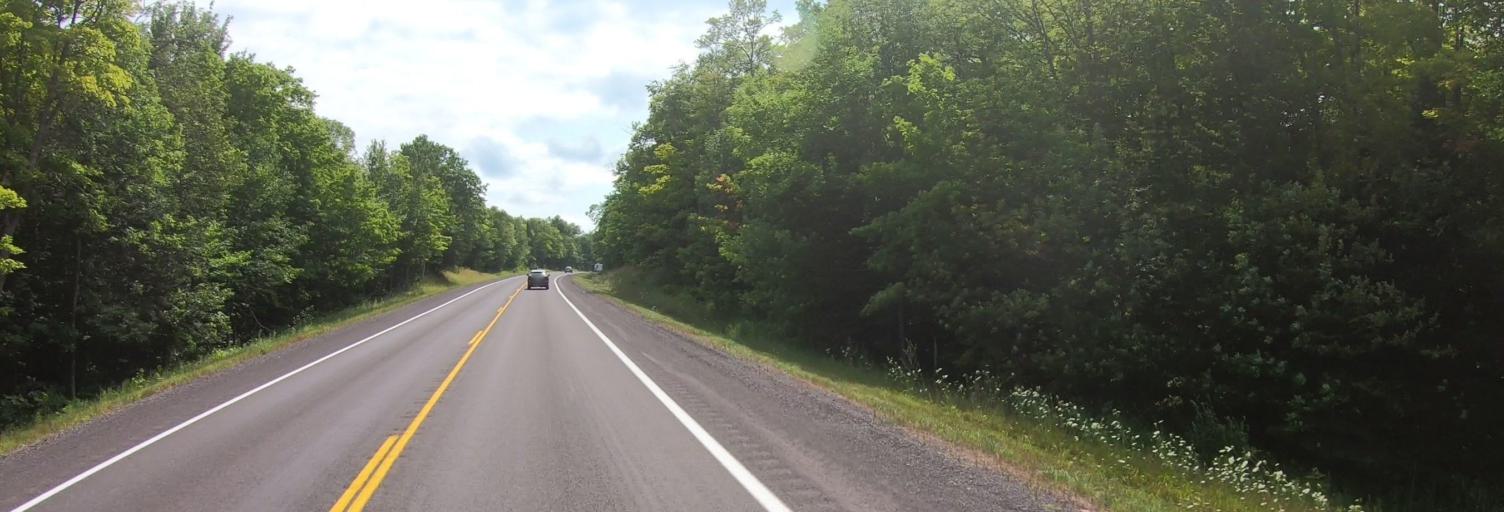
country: US
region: Michigan
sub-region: Houghton County
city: Hancock
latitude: 46.9530
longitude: -88.7817
